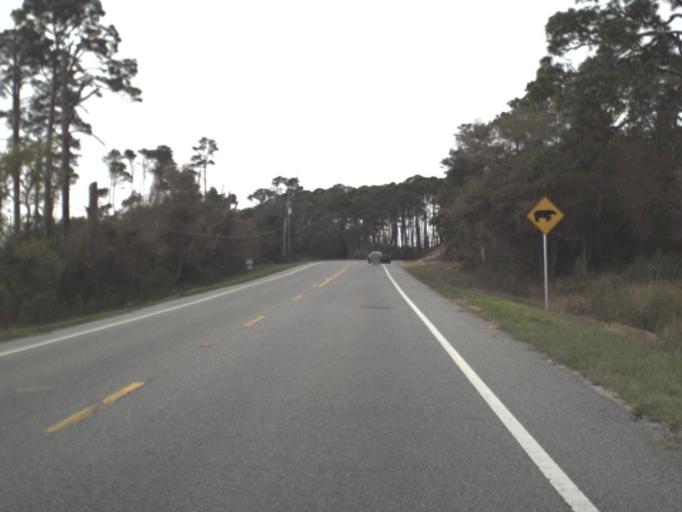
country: US
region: Florida
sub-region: Franklin County
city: Carrabelle
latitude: 29.7945
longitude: -84.7494
